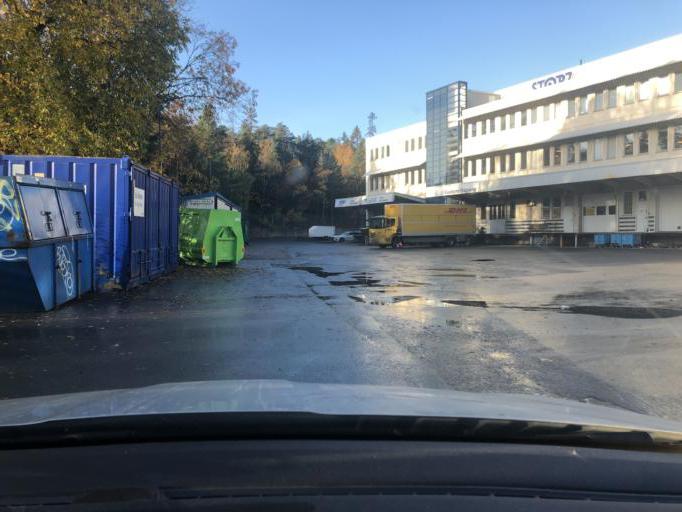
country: SE
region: Stockholm
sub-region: Huddinge Kommun
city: Segeltorp
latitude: 59.2802
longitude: 17.9188
